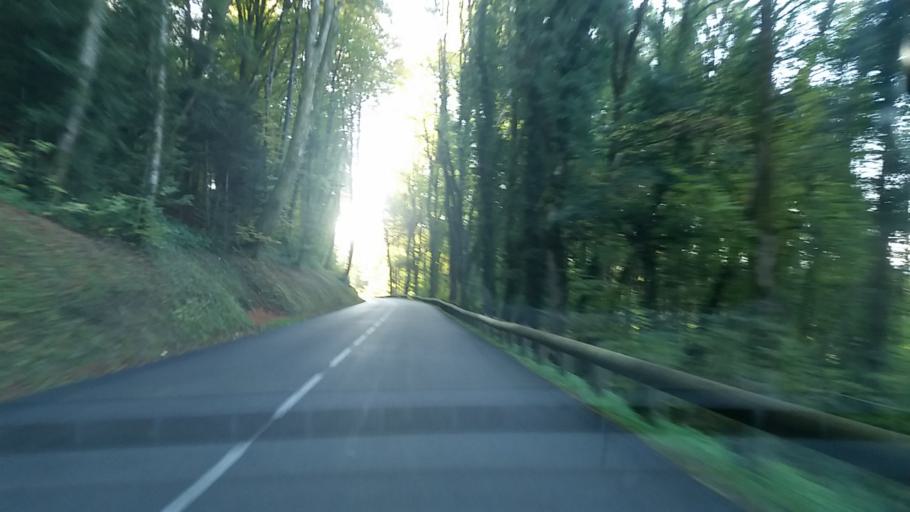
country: FR
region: Franche-Comte
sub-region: Departement du Doubs
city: Levier
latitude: 47.0024
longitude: 6.0343
